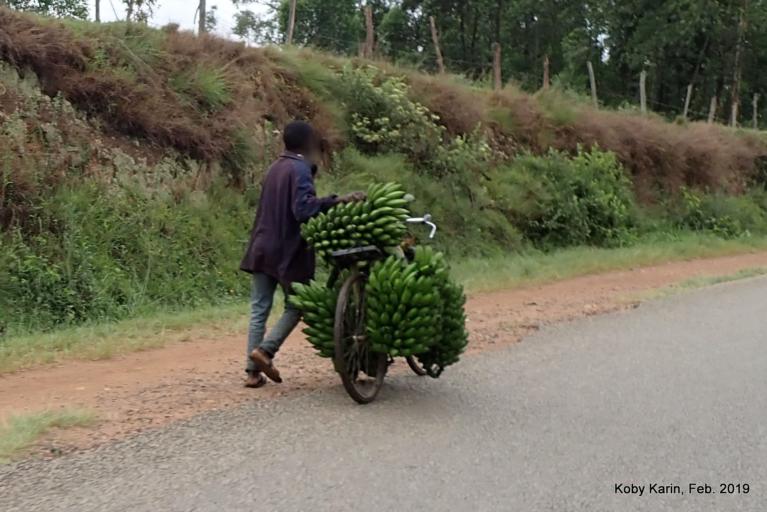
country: UG
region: Western Region
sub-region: Bushenyi District
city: Bushenyi
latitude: -0.5163
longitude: 30.1195
